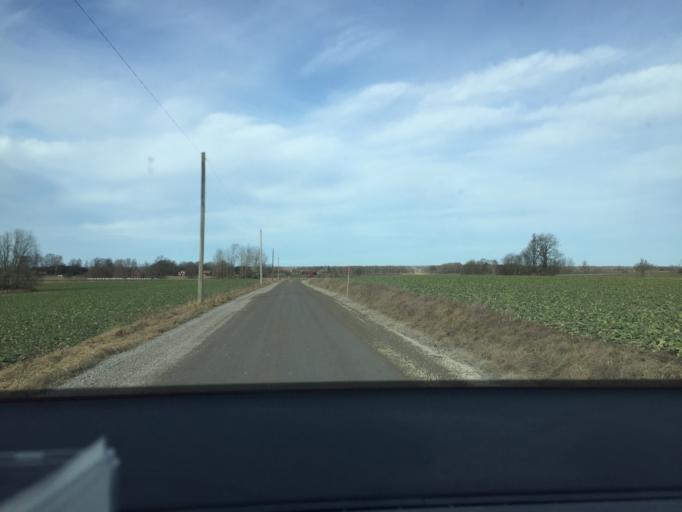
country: SE
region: OErebro
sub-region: Hallsbergs Kommun
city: Skollersta
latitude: 59.1456
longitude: 15.4139
